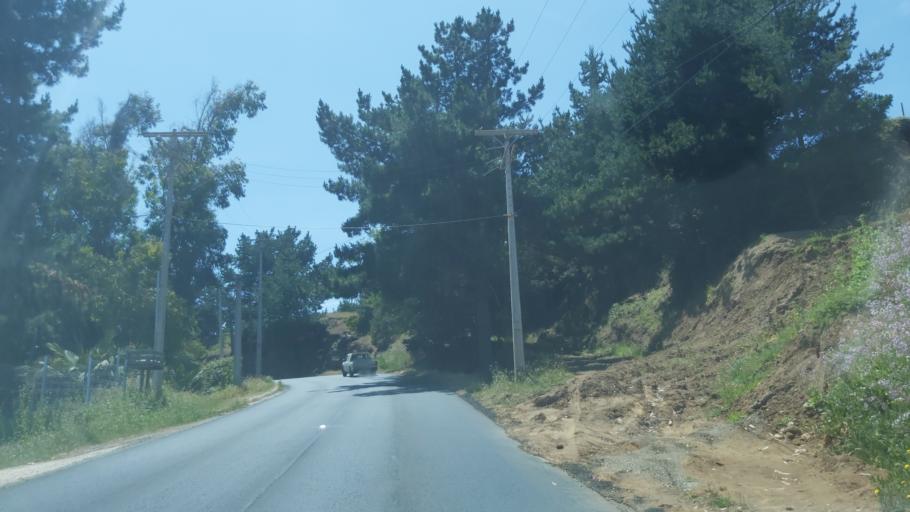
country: CL
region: Maule
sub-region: Provincia de Cauquenes
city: Cauquenes
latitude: -35.8344
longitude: -72.6212
